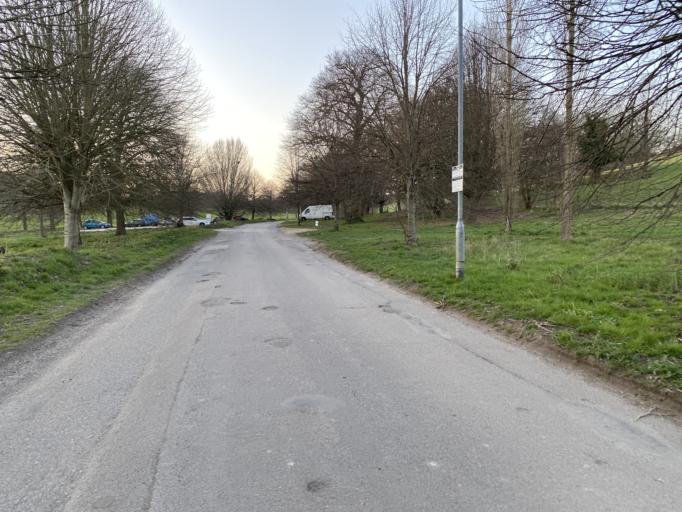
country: GB
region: England
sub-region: Brighton and Hove
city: Brighton
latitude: 50.8644
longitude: -0.0956
